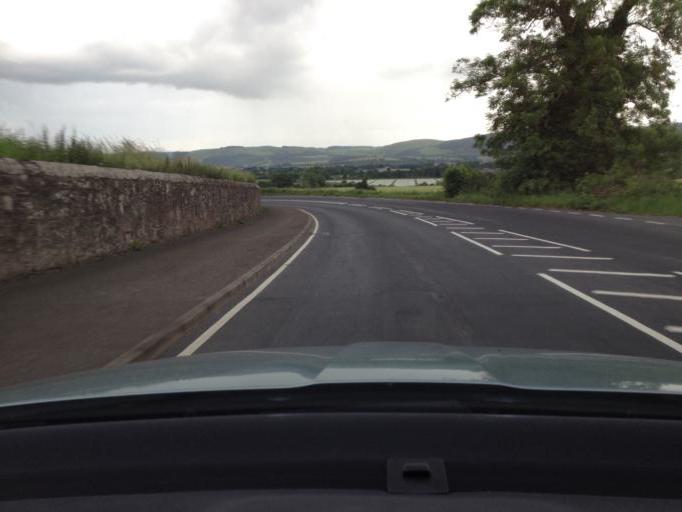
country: GB
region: Scotland
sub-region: Perth and Kinross
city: Bridge of Earn
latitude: 56.3654
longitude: -3.4279
